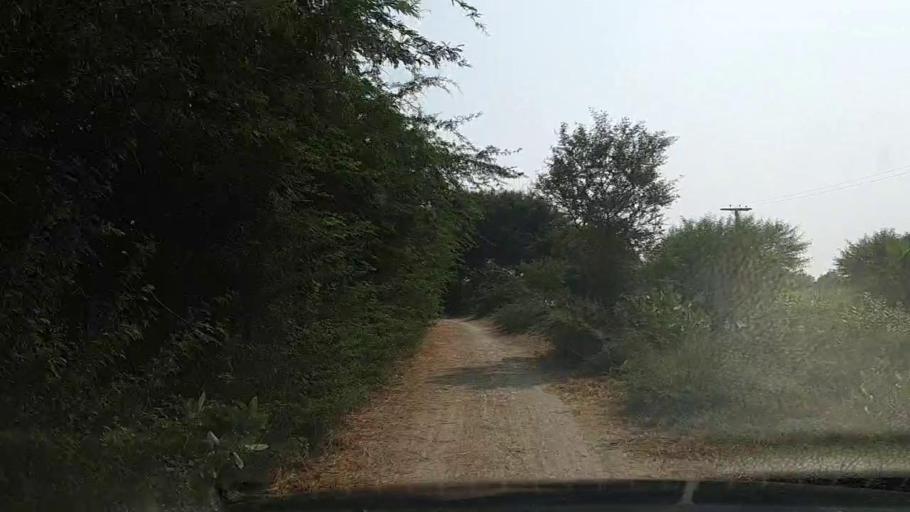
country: PK
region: Sindh
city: Mirpur Batoro
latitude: 24.6923
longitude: 68.2197
